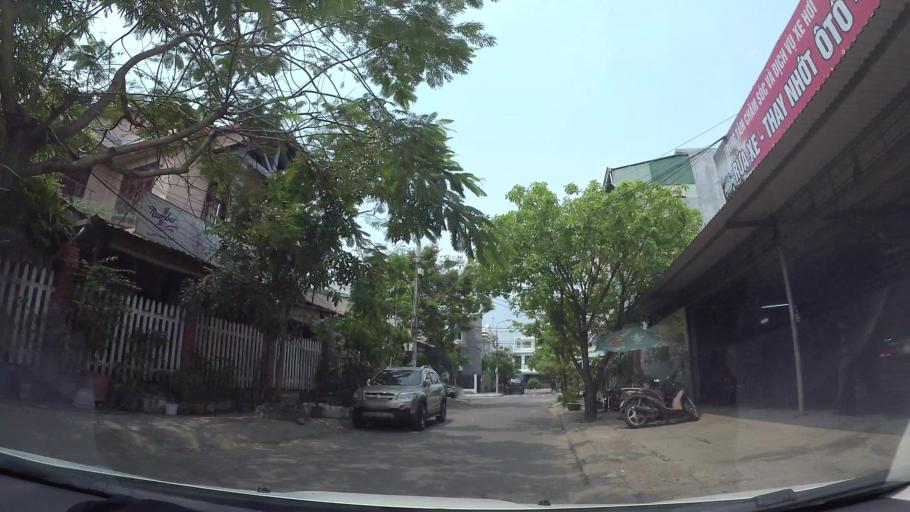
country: VN
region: Da Nang
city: Son Tra
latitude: 16.0994
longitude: 108.2489
